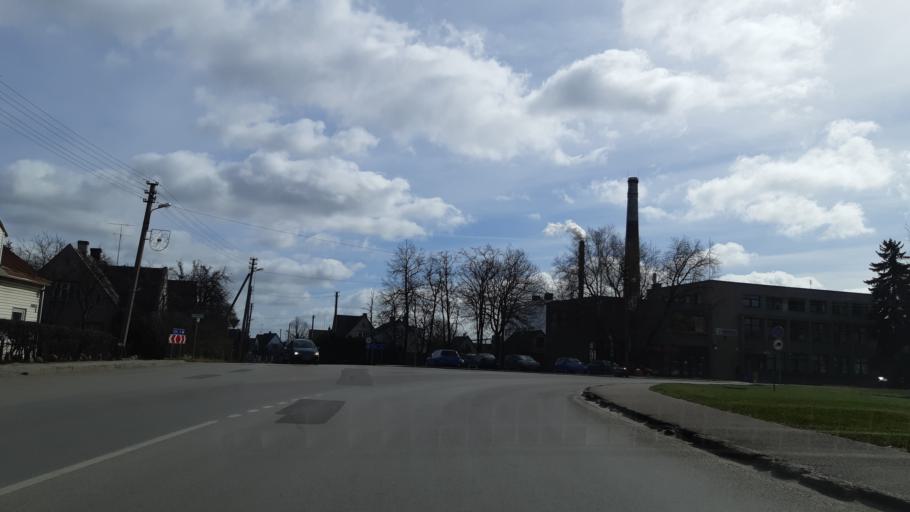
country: LT
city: Vilkaviskis
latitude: 54.6530
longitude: 23.0382
